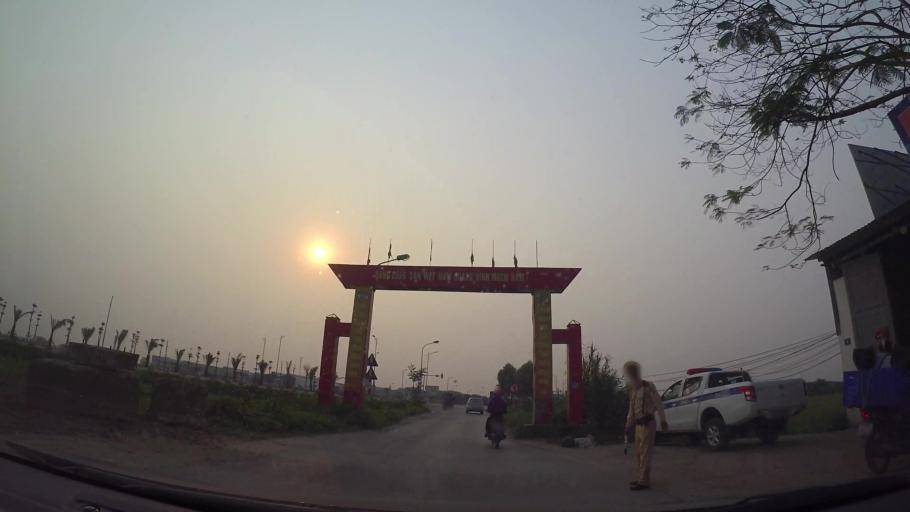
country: VN
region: Ha Noi
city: Kim Bai
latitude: 20.8719
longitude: 105.8044
